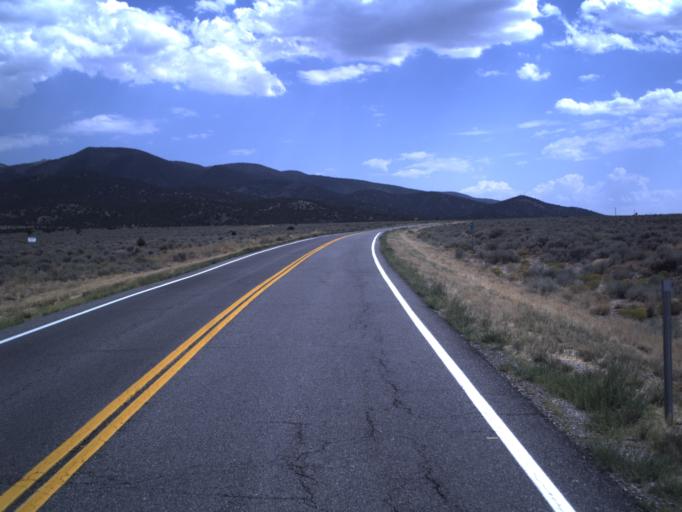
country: US
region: Utah
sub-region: Tooele County
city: Tooele
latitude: 40.3572
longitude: -112.3186
